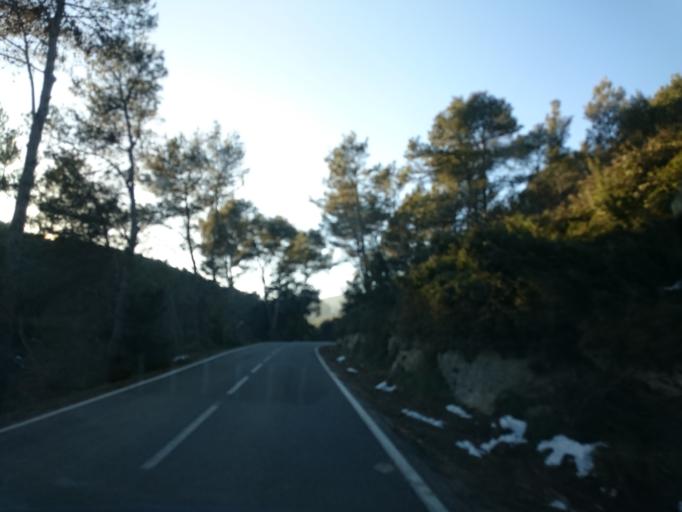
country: ES
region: Catalonia
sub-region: Provincia de Tarragona
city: la Bisbal del Penedes
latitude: 41.3755
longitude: 1.4840
